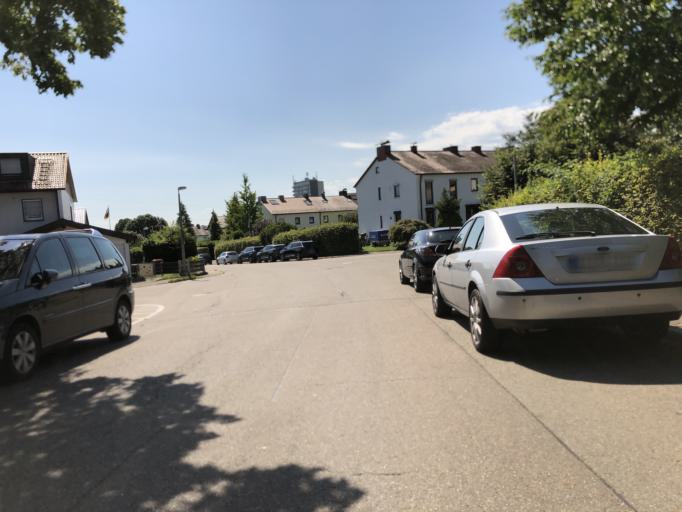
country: DE
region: Baden-Wuerttemberg
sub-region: Regierungsbezirk Stuttgart
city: Sindelfingen
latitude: 48.7191
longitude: 9.0088
